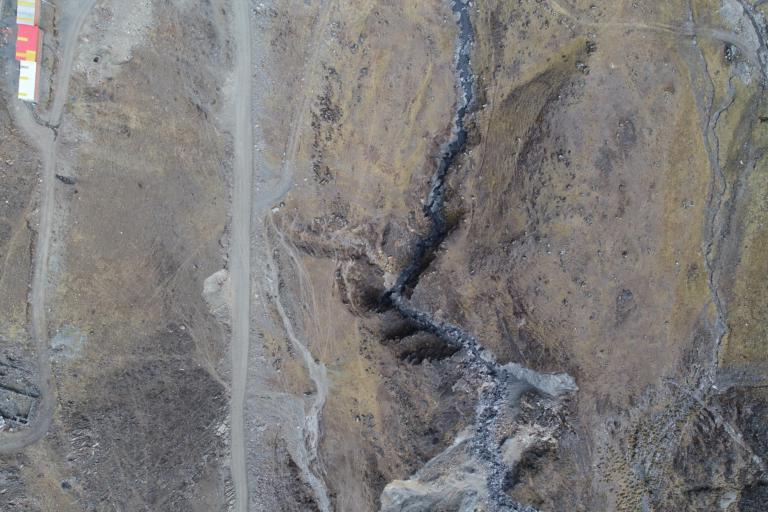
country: BO
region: La Paz
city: Sorata
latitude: -15.6707
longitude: -68.5511
